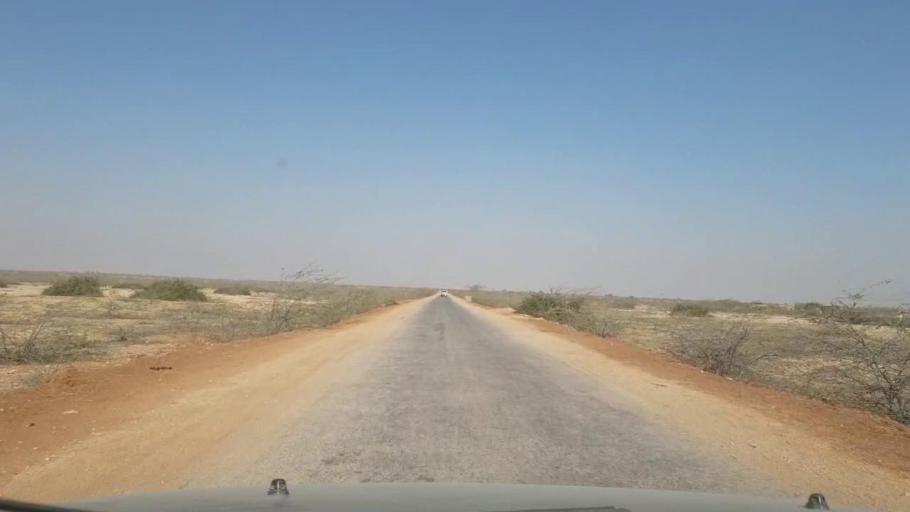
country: PK
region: Sindh
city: Thatta
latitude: 24.9388
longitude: 67.9507
